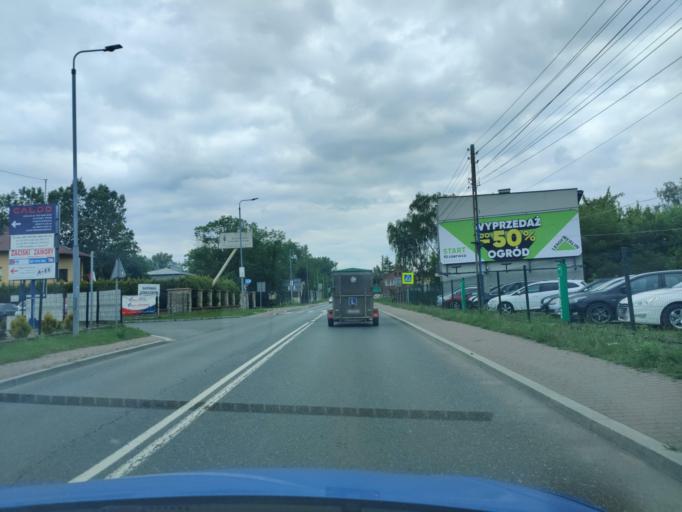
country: PL
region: Silesian Voivodeship
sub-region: Myslowice
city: Myslowice
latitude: 50.2306
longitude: 19.1631
